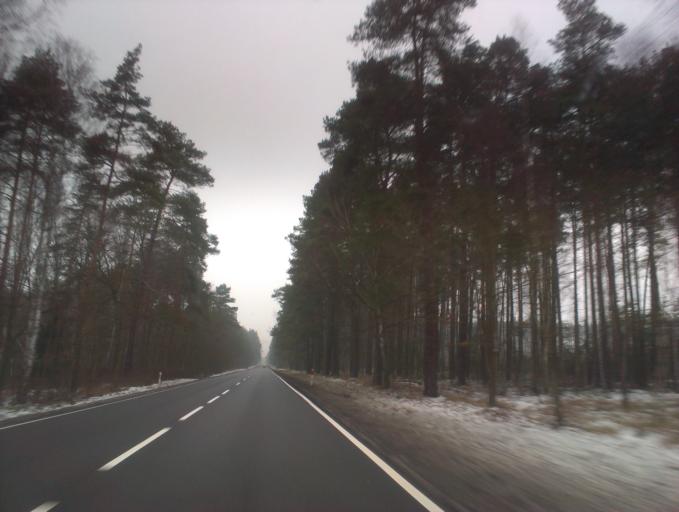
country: PL
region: Greater Poland Voivodeship
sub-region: Powiat pilski
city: Pila
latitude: 53.2410
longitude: 16.7911
